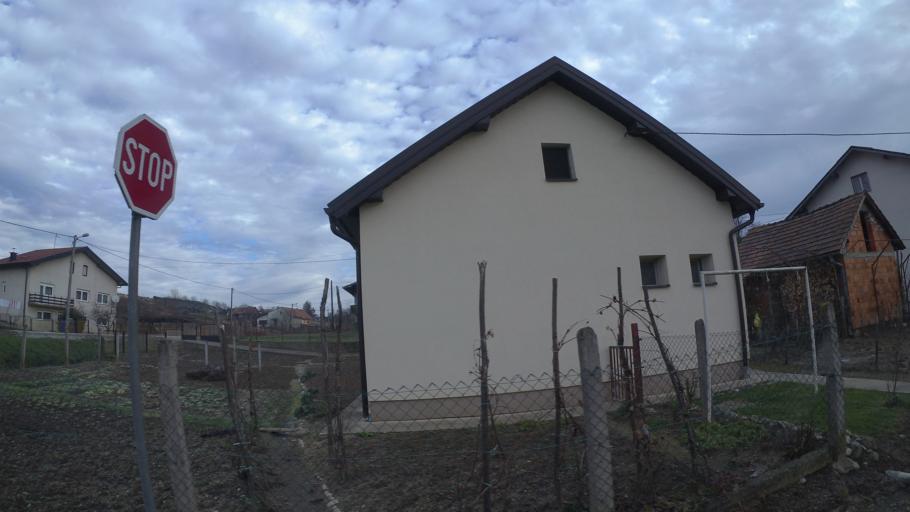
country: HR
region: Karlovacka
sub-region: Grad Karlovac
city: Karlovac
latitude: 45.4833
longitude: 15.5303
